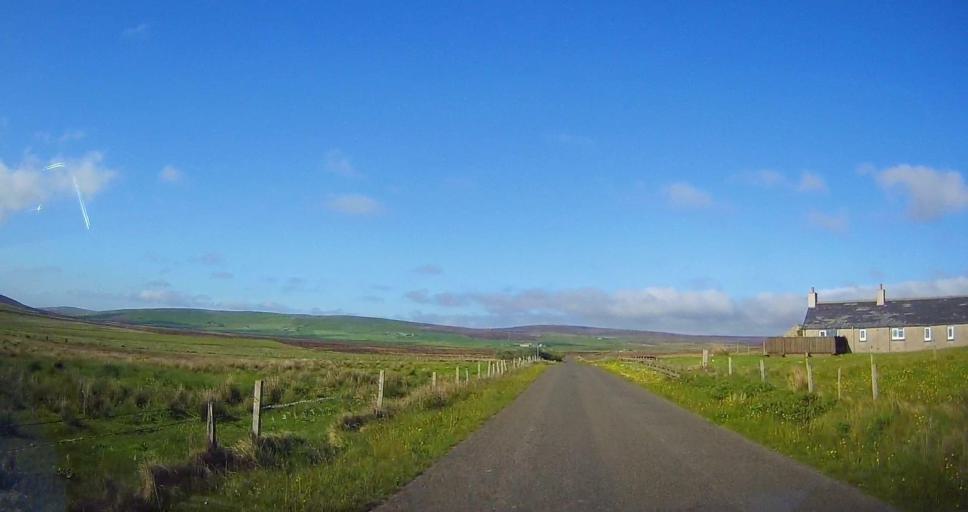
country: GB
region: Scotland
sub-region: Orkney Islands
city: Stromness
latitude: 59.0759
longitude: -3.2038
